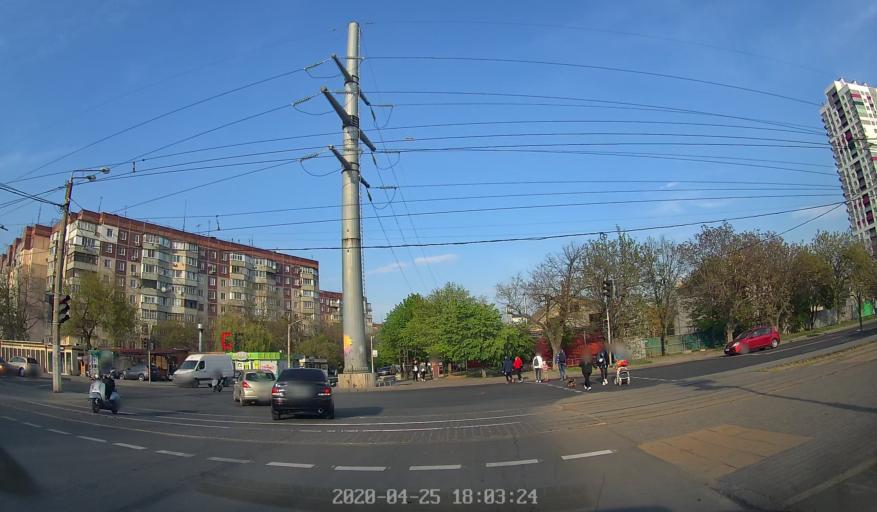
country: GR
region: South Aegean
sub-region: Nomos Kykladon
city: Serifos
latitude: 37.1261
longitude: 24.5837
